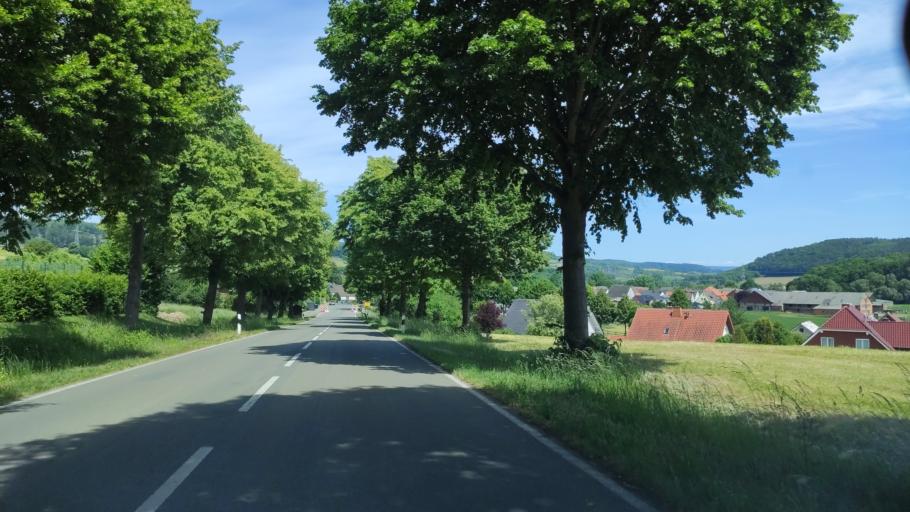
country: DE
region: North Rhine-Westphalia
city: Brakel
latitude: 51.7073
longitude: 9.2347
